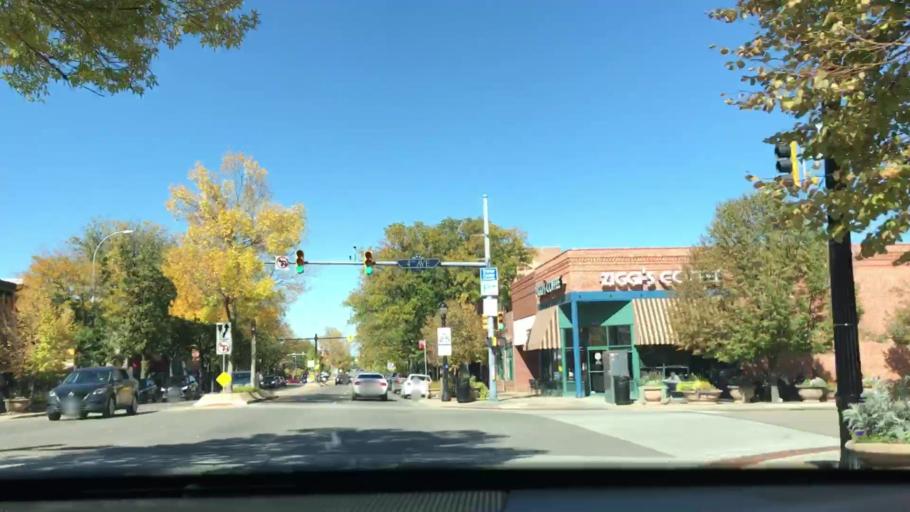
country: US
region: Colorado
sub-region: Boulder County
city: Longmont
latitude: 40.1655
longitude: -105.1025
